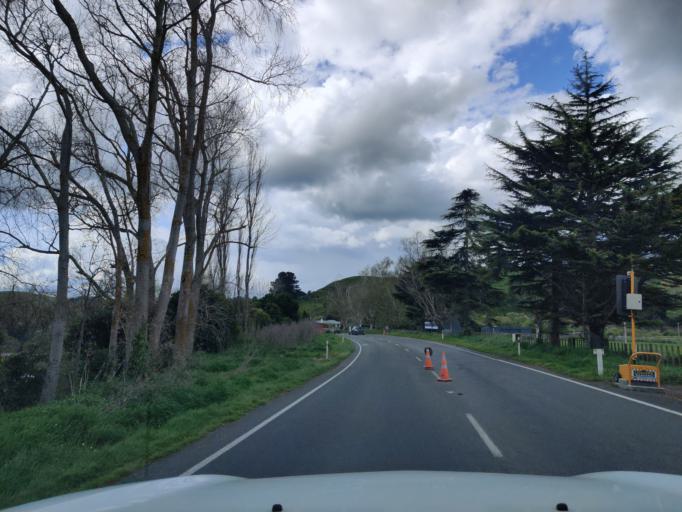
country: NZ
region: Manawatu-Wanganui
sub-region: Wanganui District
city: Wanganui
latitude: -39.8753
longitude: 175.1113
